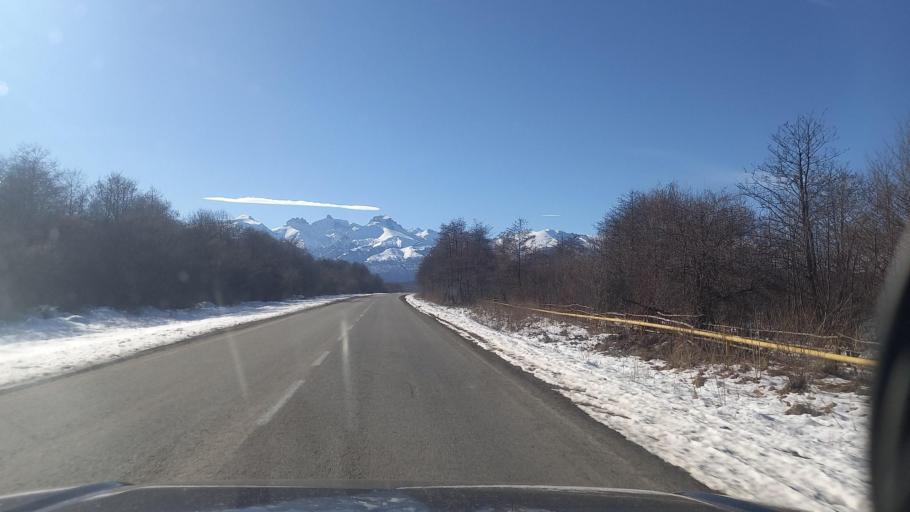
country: RU
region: North Ossetia
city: Chikola
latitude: 43.1558
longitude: 43.8445
